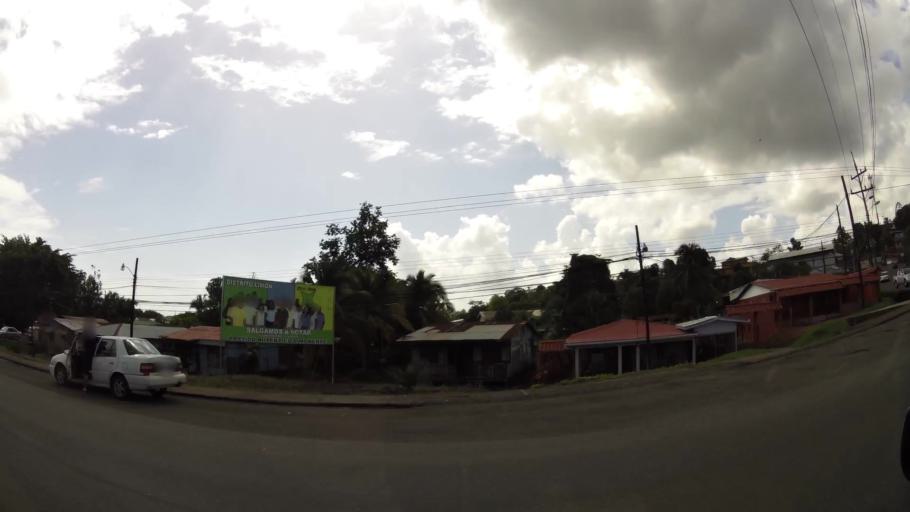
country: CR
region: Limon
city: Limon
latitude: 9.9852
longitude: -83.0534
